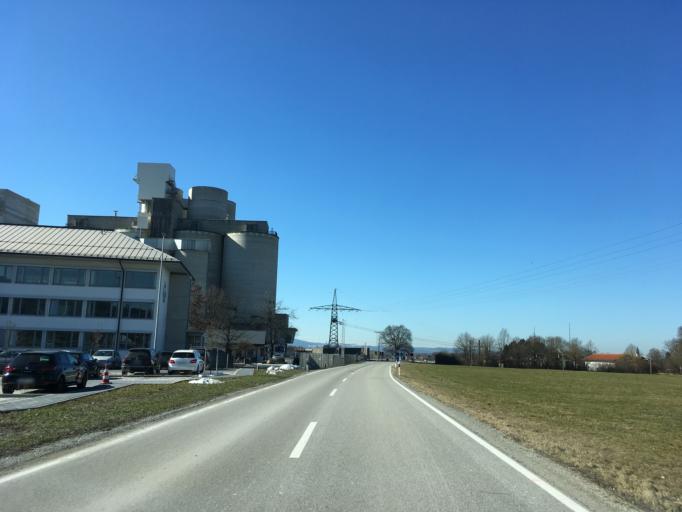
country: DE
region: Bavaria
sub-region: Upper Bavaria
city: Rohrdorf
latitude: 47.7932
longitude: 12.1835
